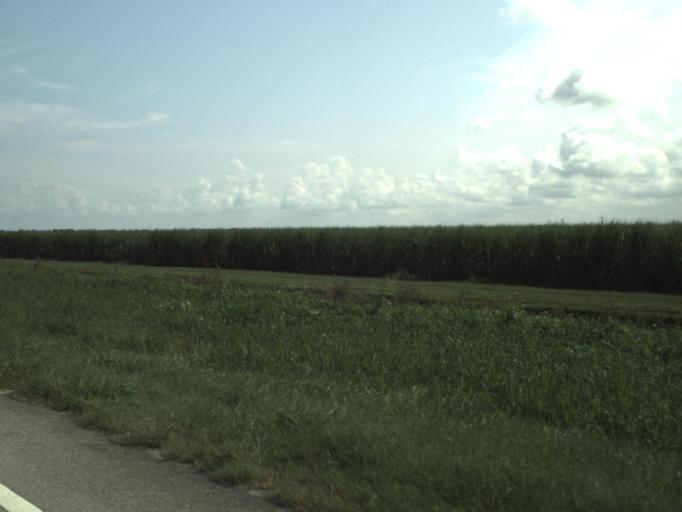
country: US
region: Florida
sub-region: Palm Beach County
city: Pahokee
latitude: 26.7790
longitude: -80.6892
